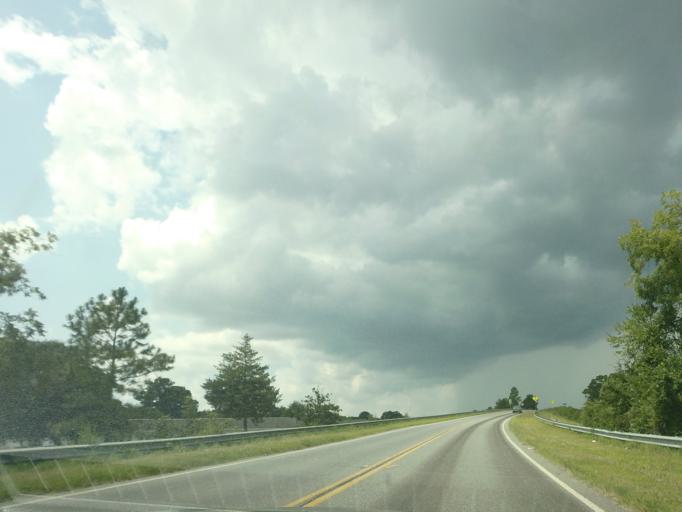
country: US
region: Georgia
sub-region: Bleckley County
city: Cochran
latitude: 32.3768
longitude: -83.3435
